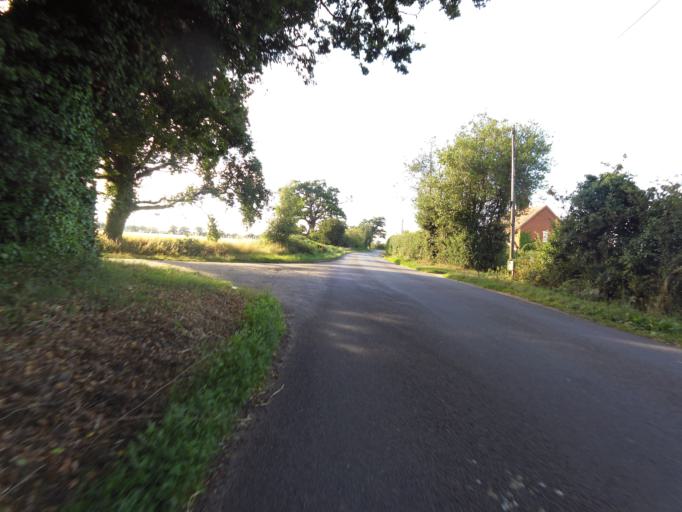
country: GB
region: England
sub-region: Suffolk
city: Kesgrave
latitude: 52.0191
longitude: 1.2175
